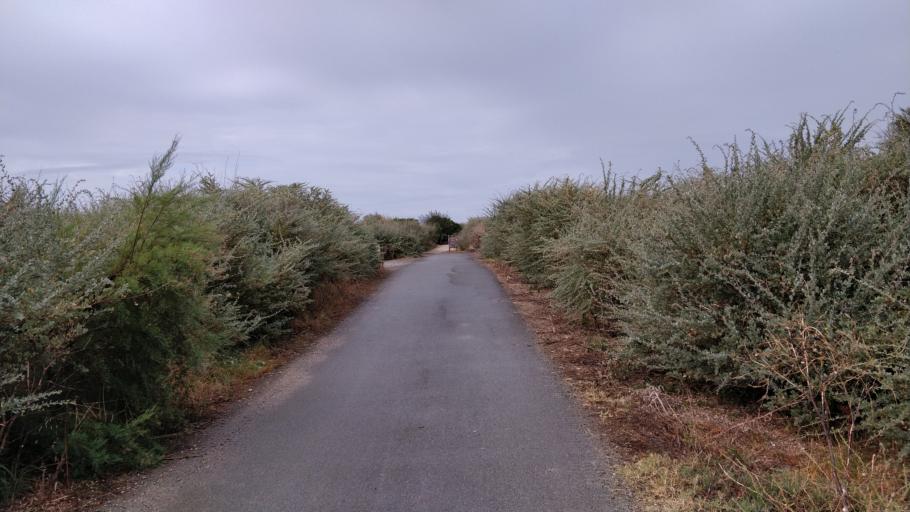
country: FR
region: Poitou-Charentes
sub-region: Departement de la Charente-Maritime
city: La Couarde-sur-Mer
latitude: 46.2237
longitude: -1.4191
